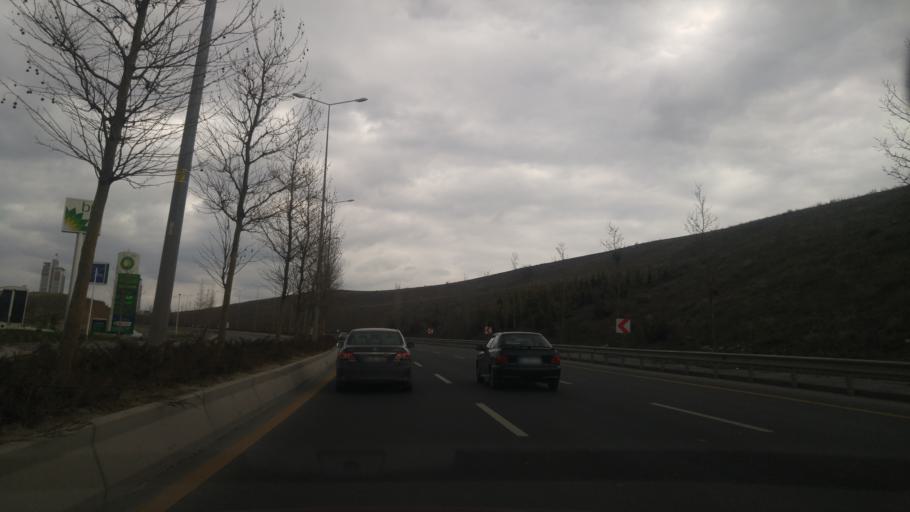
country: TR
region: Ankara
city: Mamak
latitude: 39.8845
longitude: 32.9201
